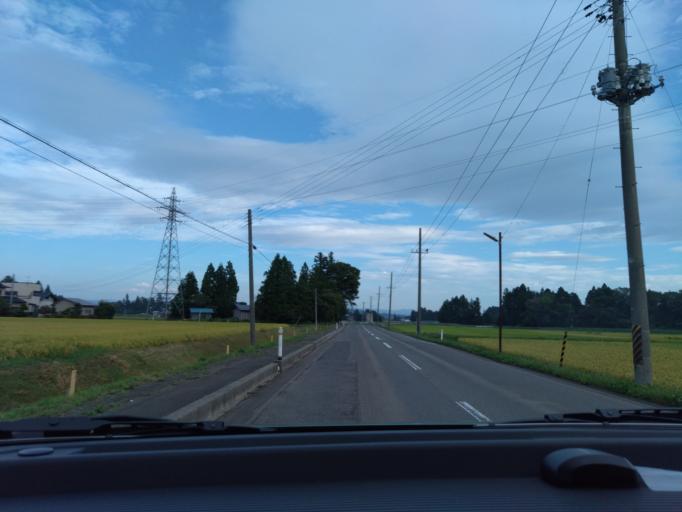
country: JP
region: Iwate
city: Kitakami
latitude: 39.3282
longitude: 141.0580
